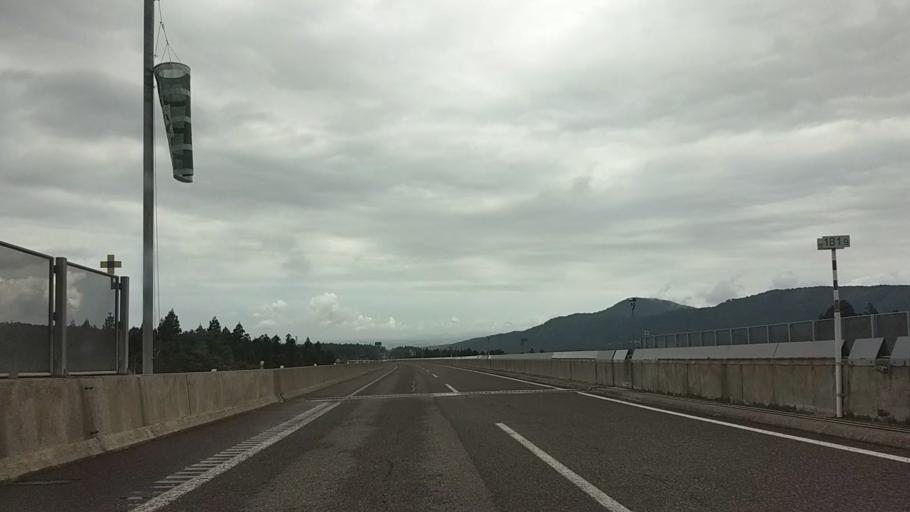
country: JP
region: Niigata
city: Arai
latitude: 36.9468
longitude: 138.2148
